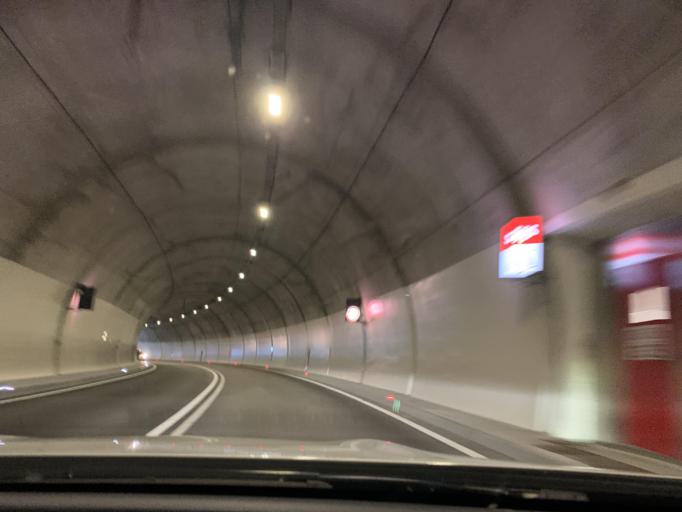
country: IT
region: Trentino-Alto Adige
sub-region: Bolzano
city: Cornedo All'Isarco
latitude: 46.4689
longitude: 11.4088
